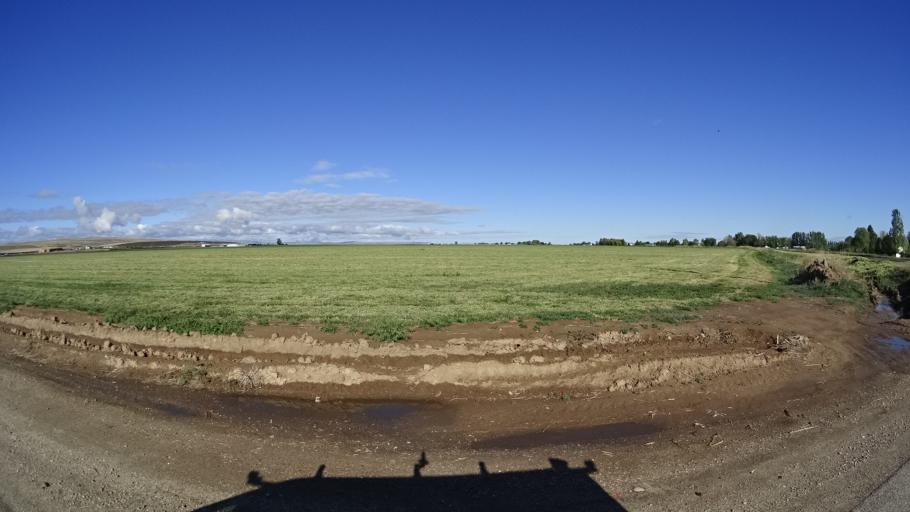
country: US
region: Idaho
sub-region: Ada County
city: Kuna
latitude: 43.4703
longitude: -116.4136
